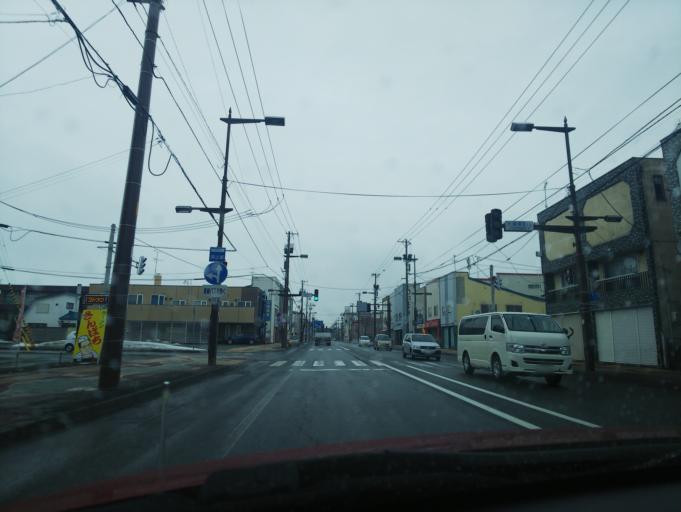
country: JP
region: Hokkaido
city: Nayoro
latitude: 44.1738
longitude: 142.3930
